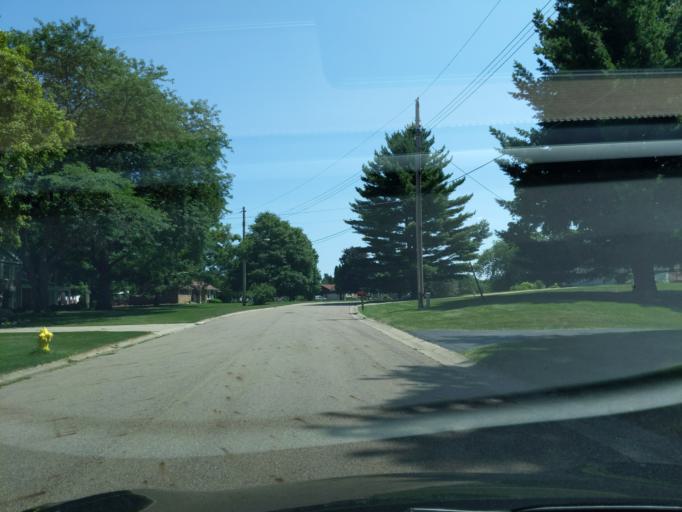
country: US
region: Michigan
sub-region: Eaton County
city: Waverly
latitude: 42.7683
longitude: -84.6158
